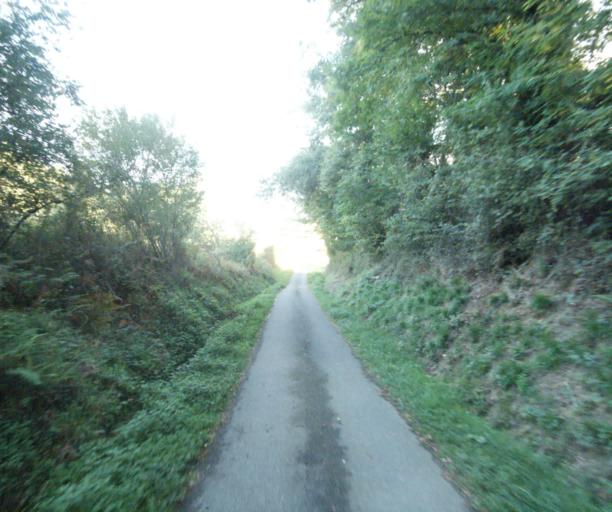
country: FR
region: Midi-Pyrenees
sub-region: Departement du Gers
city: Le Houga
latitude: 43.8307
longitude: -0.1102
